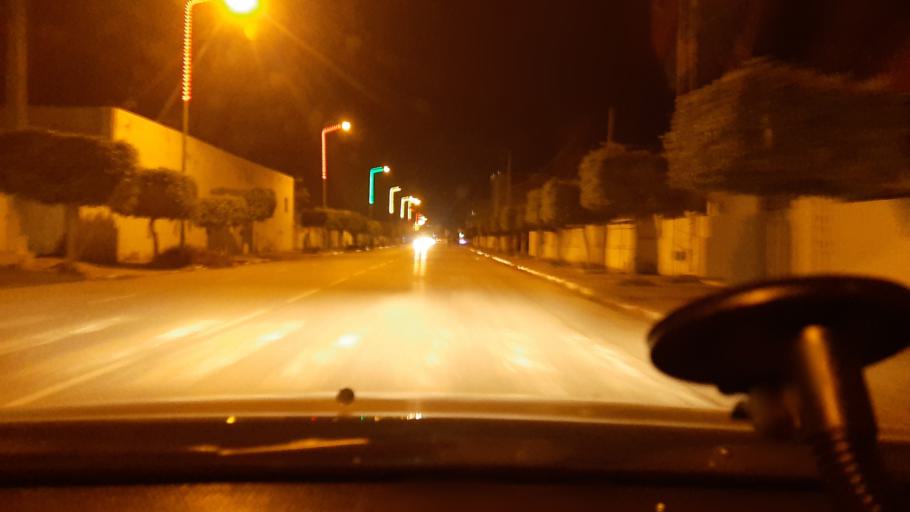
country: TN
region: Safaqis
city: Sfax
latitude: 34.7766
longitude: 10.7273
